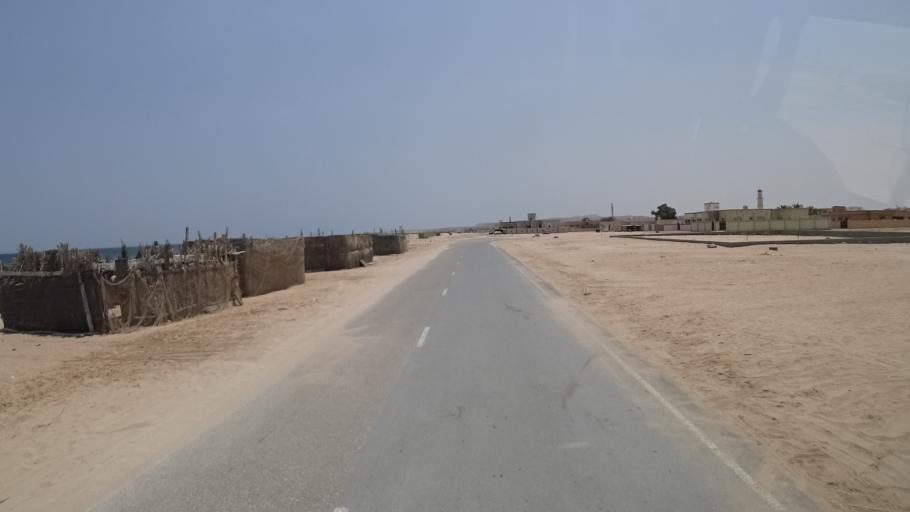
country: OM
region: Ash Sharqiyah
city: Sur
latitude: 22.5225
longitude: 59.7984
